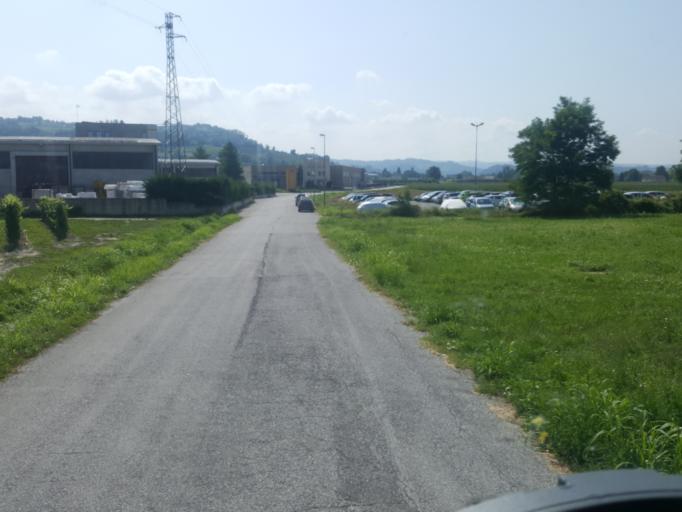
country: IT
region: Piedmont
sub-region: Provincia di Cuneo
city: Narzole
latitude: 44.5953
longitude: 7.8957
